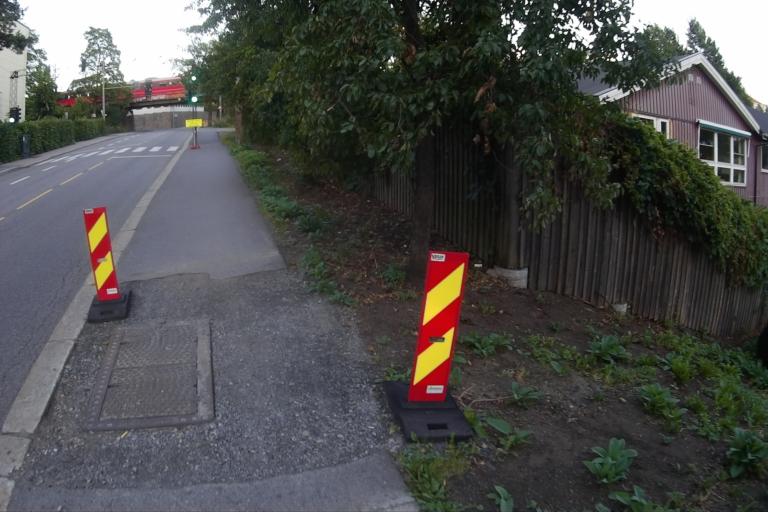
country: NO
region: Oslo
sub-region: Oslo
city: Oslo
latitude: 59.9249
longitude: 10.7806
